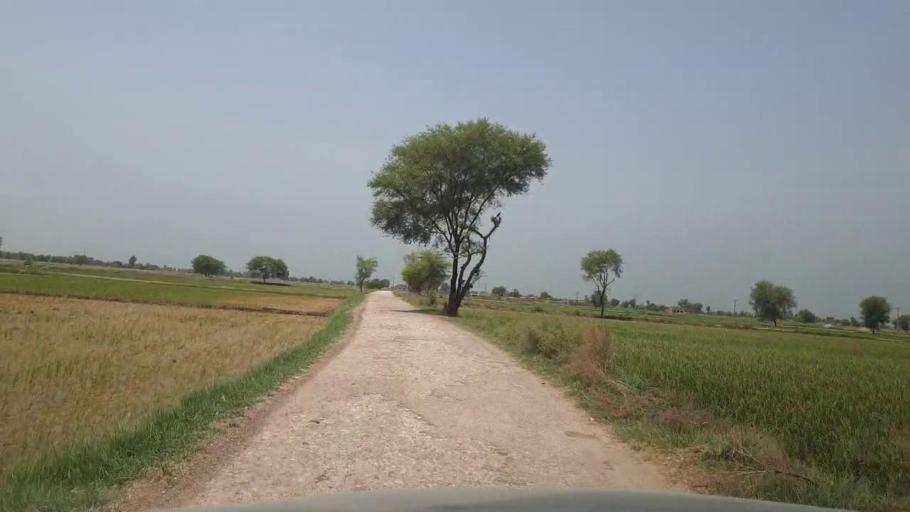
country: PK
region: Sindh
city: Garhi Yasin
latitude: 27.9206
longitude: 68.3691
